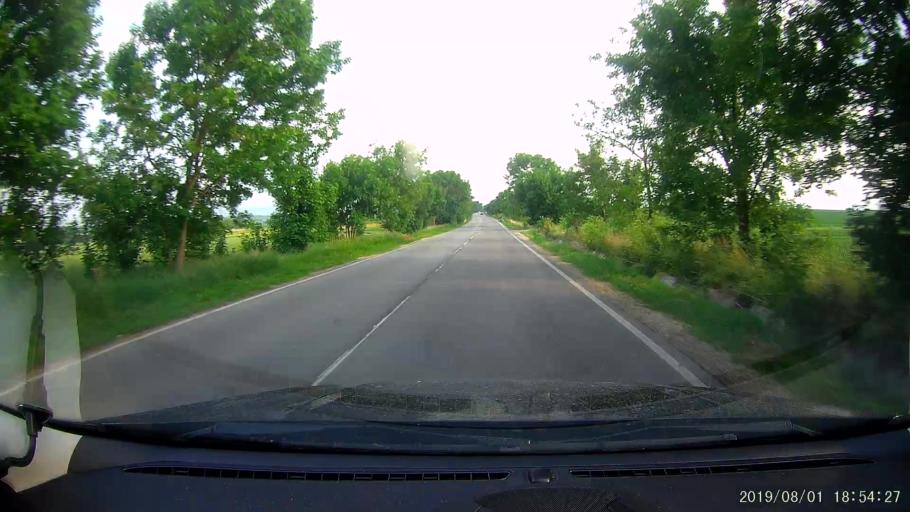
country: BG
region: Shumen
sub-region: Obshtina Shumen
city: Shumen
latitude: 43.1982
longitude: 27.0018
